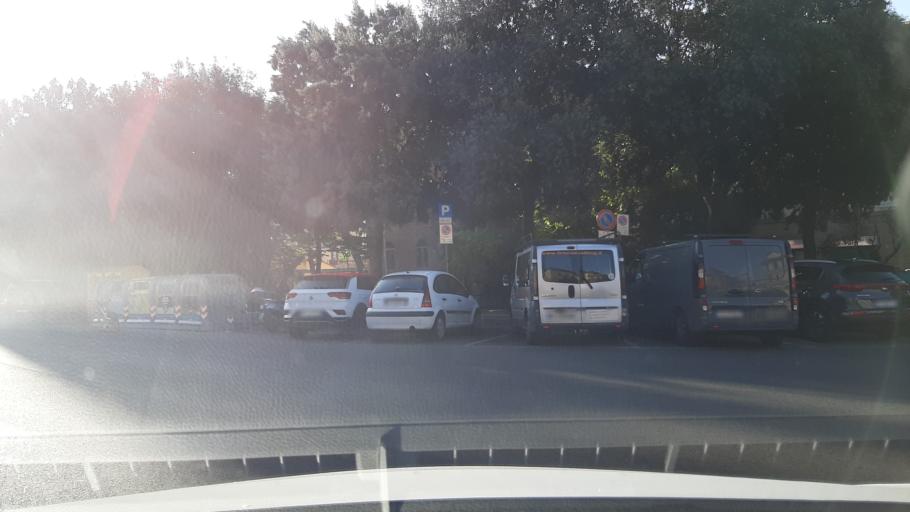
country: IT
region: Tuscany
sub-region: Province of Florence
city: Fiesole
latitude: 43.7843
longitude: 11.2825
